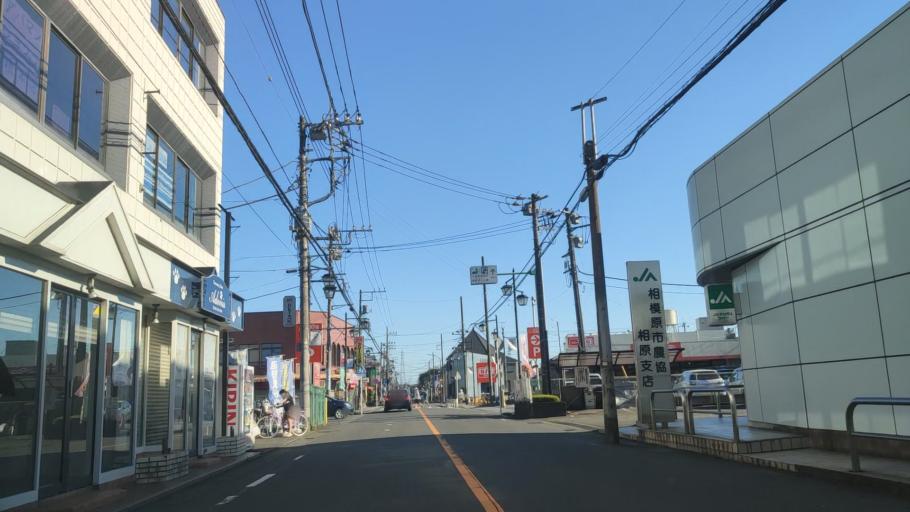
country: JP
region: Tokyo
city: Hachioji
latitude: 35.5966
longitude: 139.3207
